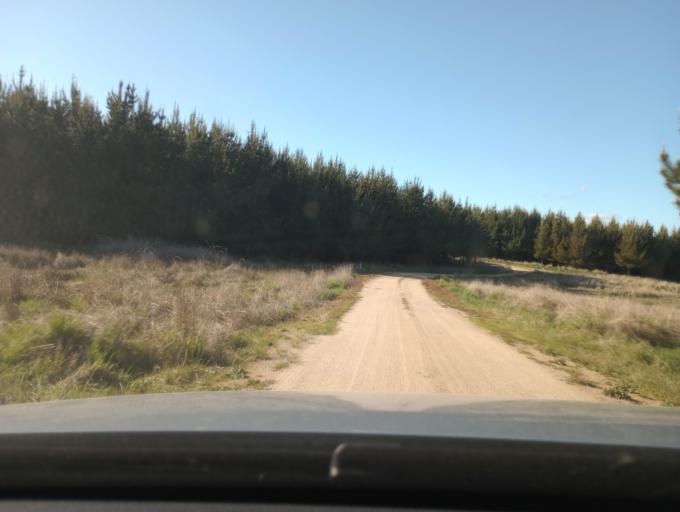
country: AU
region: New South Wales
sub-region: Blayney
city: Millthorpe
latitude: -33.4112
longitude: 149.3071
